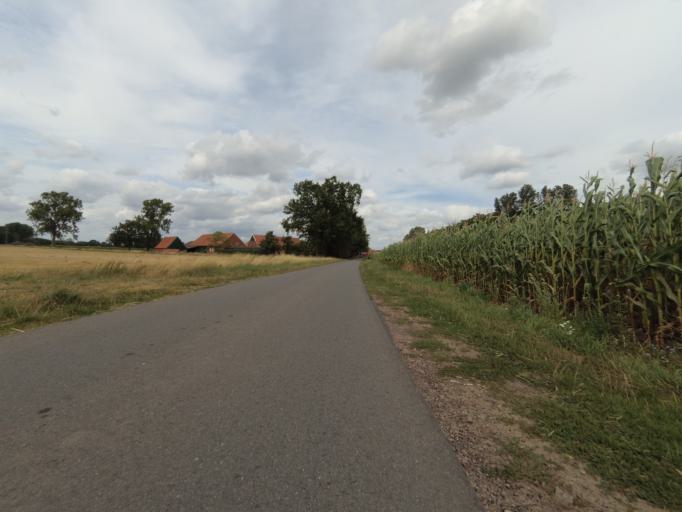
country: DE
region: North Rhine-Westphalia
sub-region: Regierungsbezirk Munster
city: Ahaus
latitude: 52.1162
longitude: 7.0146
